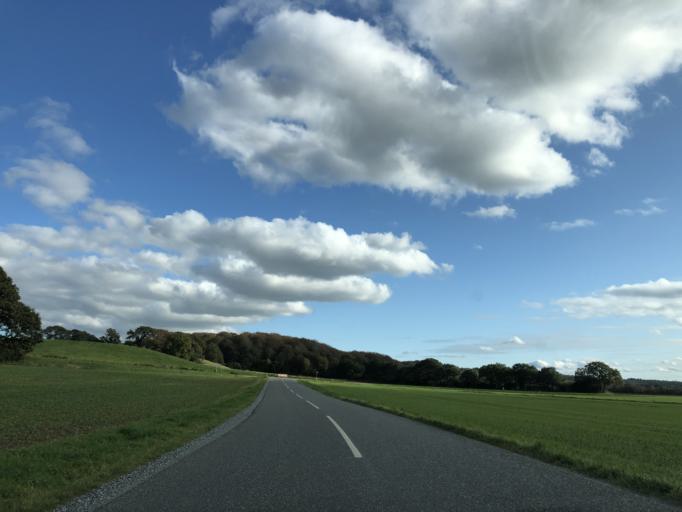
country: DK
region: Central Jutland
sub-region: Silkeborg Kommune
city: Svejbaek
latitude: 56.2500
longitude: 9.6755
